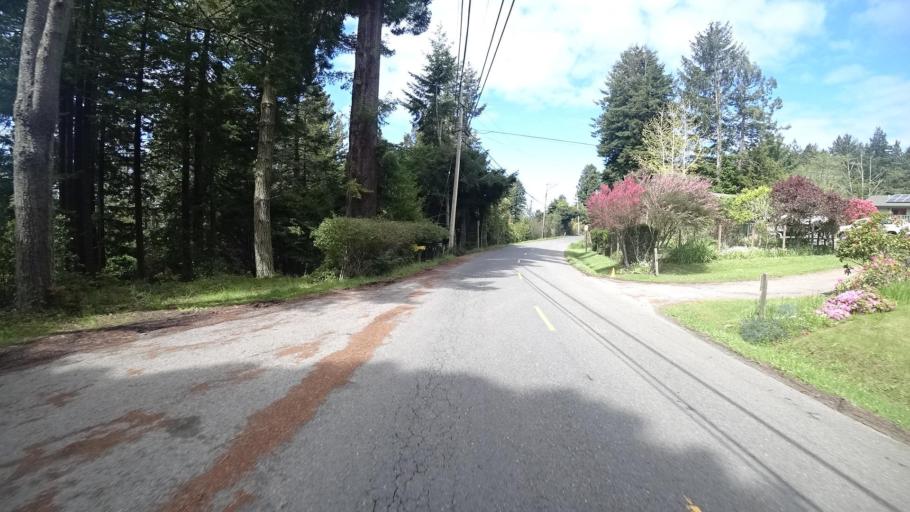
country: US
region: California
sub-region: Humboldt County
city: Bayside
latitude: 40.8668
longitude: -124.0539
